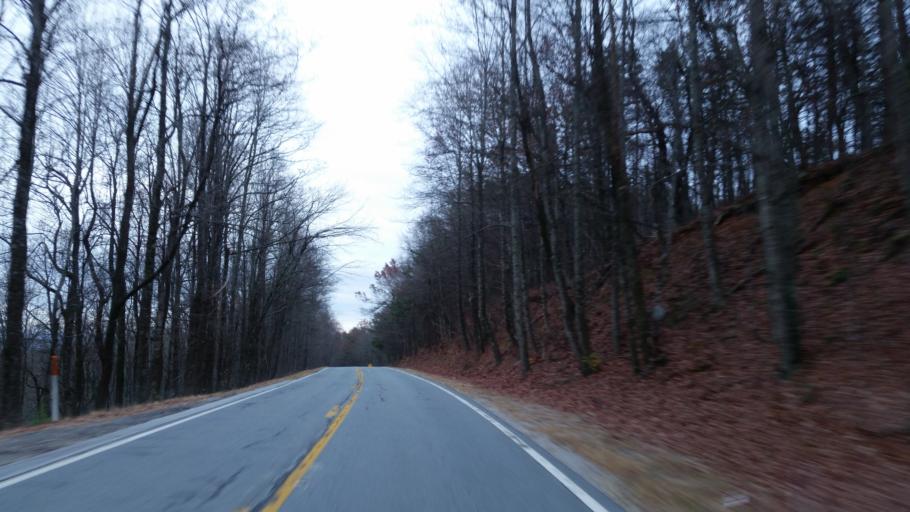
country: US
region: Georgia
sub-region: Pickens County
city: Jasper
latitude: 34.5383
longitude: -84.3120
